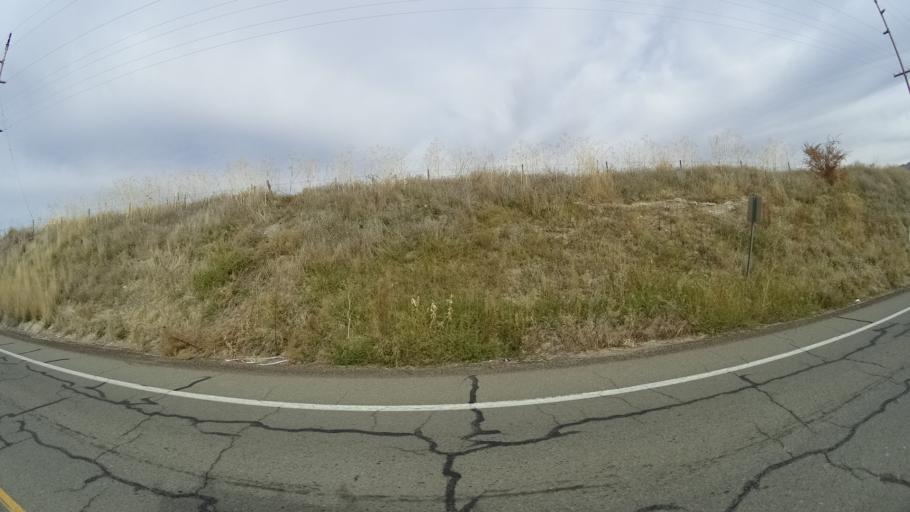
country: US
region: California
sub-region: Siskiyou County
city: Montague
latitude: 41.7056
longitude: -122.5423
